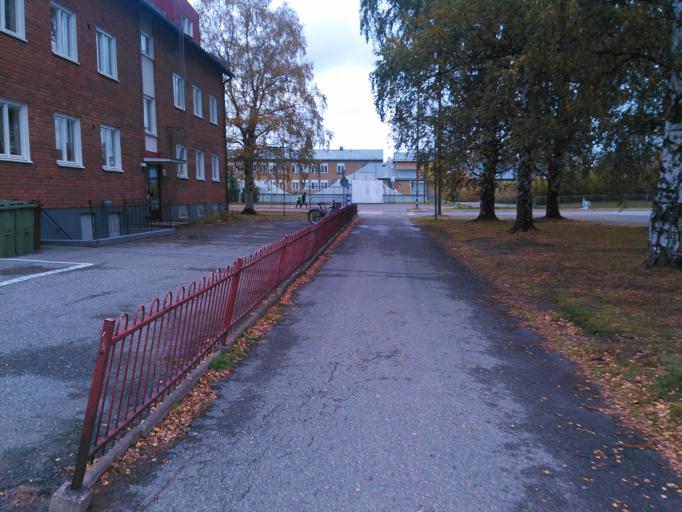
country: SE
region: Vaesterbotten
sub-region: Umea Kommun
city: Umea
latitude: 63.8185
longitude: 20.2465
